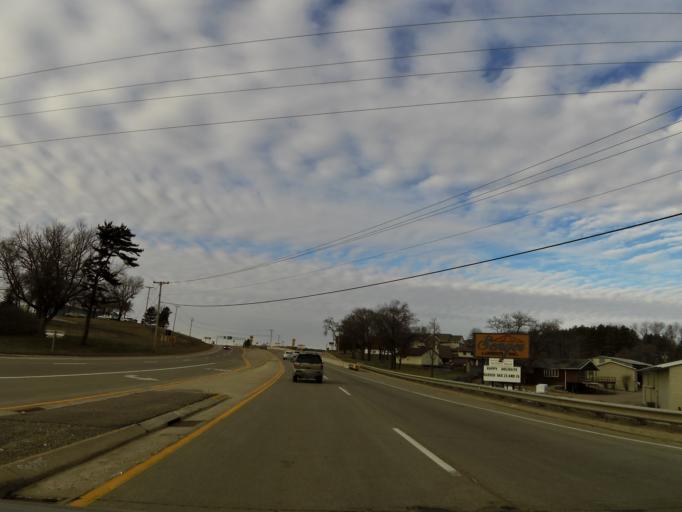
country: US
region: Wisconsin
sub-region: Sauk County
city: West Baraboo
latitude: 43.4855
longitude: -89.7733
